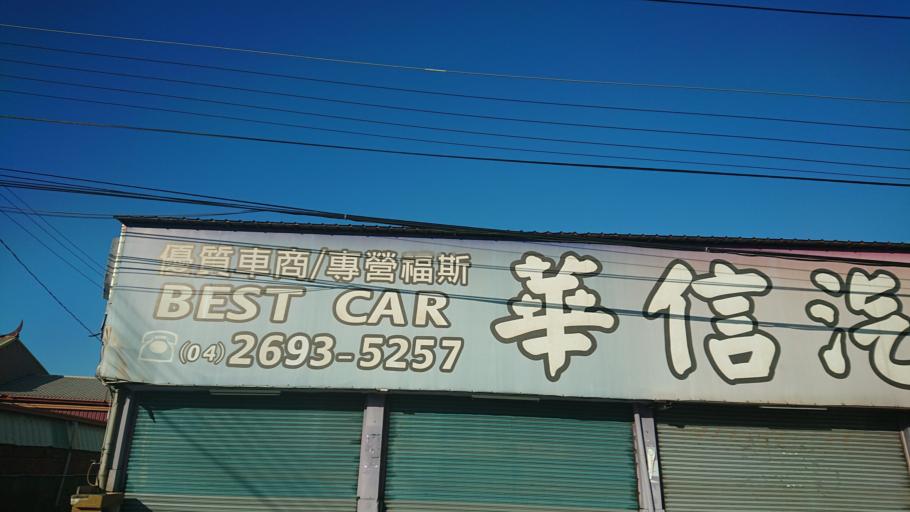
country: TW
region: Taiwan
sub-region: Changhua
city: Chang-hua
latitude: 24.1205
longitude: 120.5722
